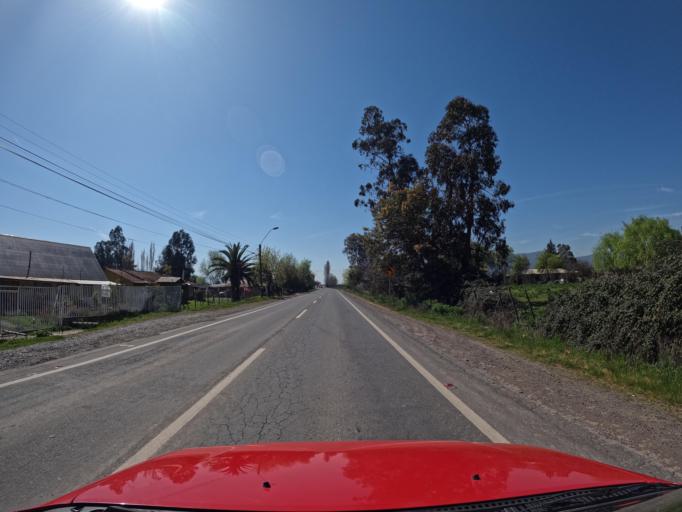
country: CL
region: Maule
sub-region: Provincia de Curico
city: Rauco
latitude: -35.0384
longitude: -71.4513
